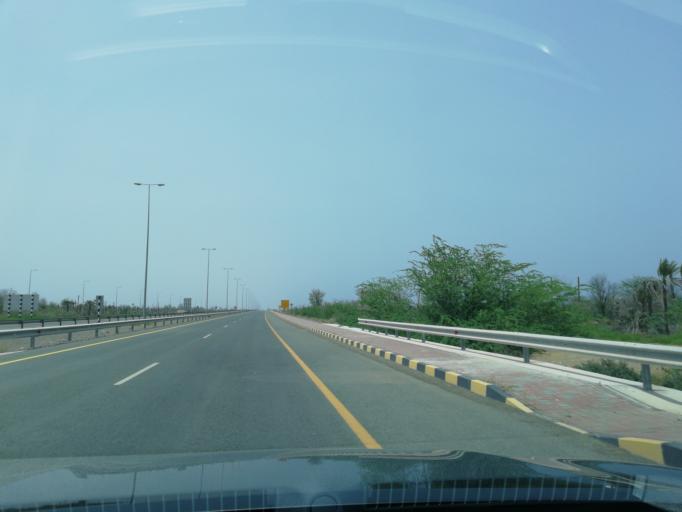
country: OM
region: Al Batinah
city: Shinas
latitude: 24.6441
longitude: 56.5188
